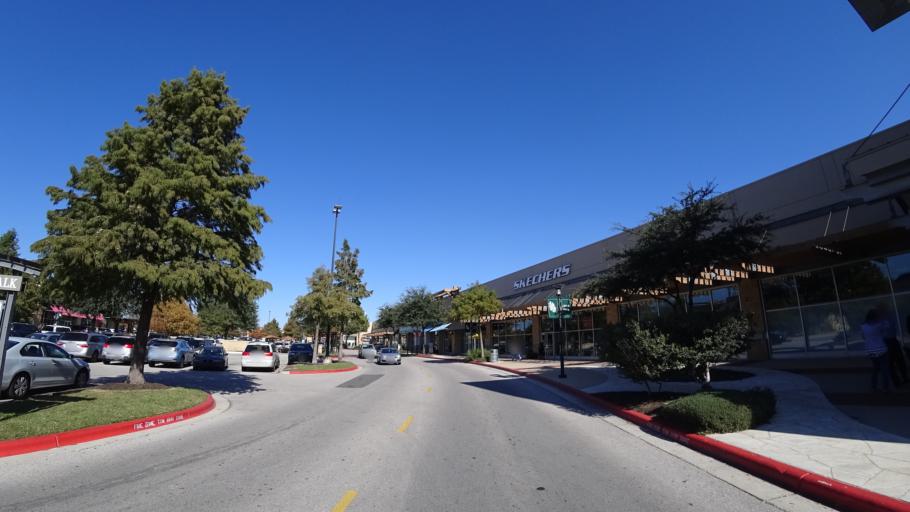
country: US
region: Texas
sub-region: Williamson County
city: Jollyville
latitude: 30.3890
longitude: -97.7329
